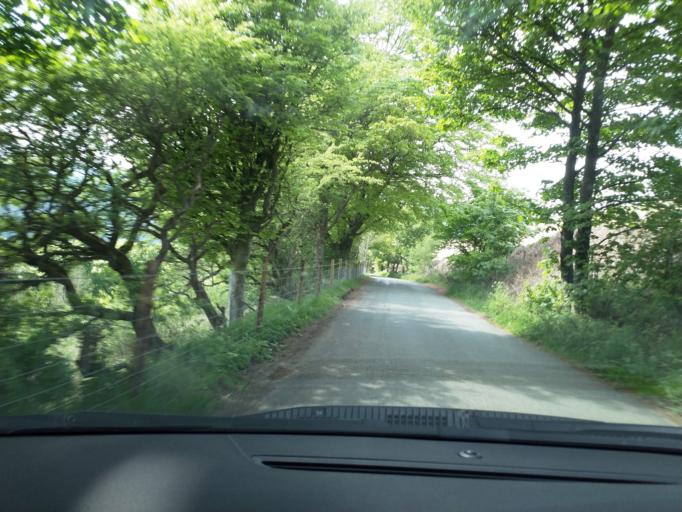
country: GB
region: England
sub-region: Derbyshire
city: Hathersage
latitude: 53.3554
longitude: -1.6877
